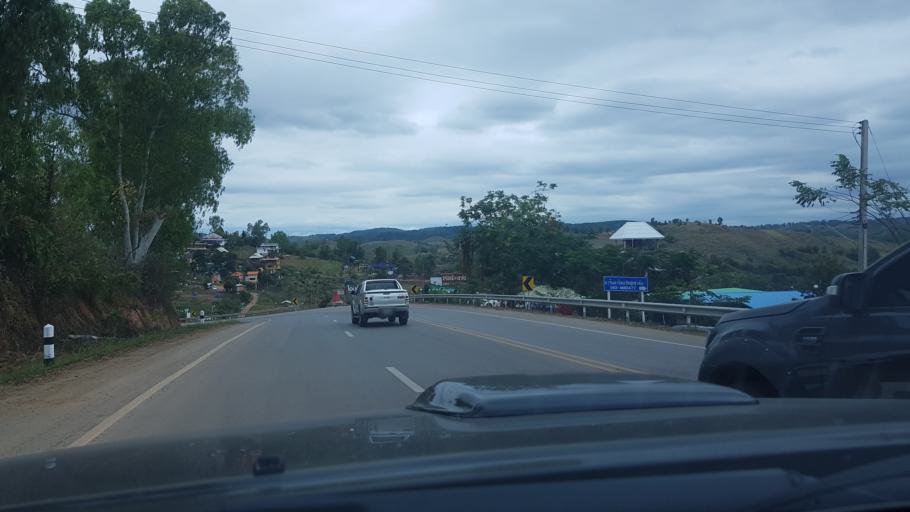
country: TH
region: Phetchabun
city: Khao Kho
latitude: 16.5661
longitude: 101.0072
